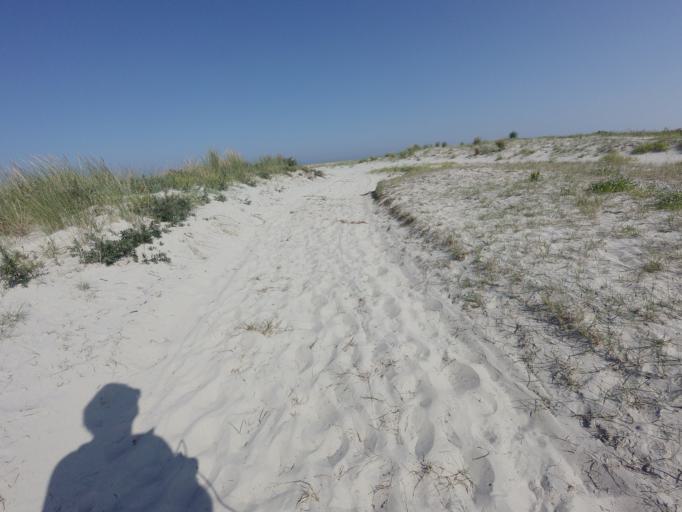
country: NL
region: Friesland
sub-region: Gemeente Schiermonnikoog
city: Schiermonnikoog
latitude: 53.5013
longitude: 6.2455
